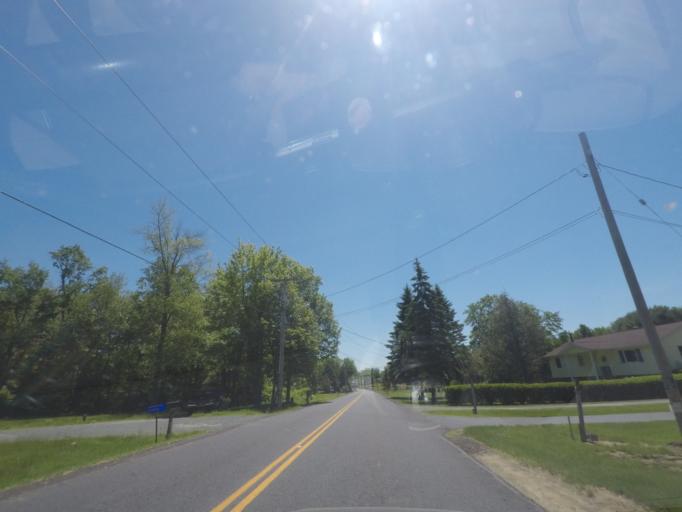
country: US
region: New York
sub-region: Saratoga County
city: Mechanicville
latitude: 42.9426
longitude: -73.7061
